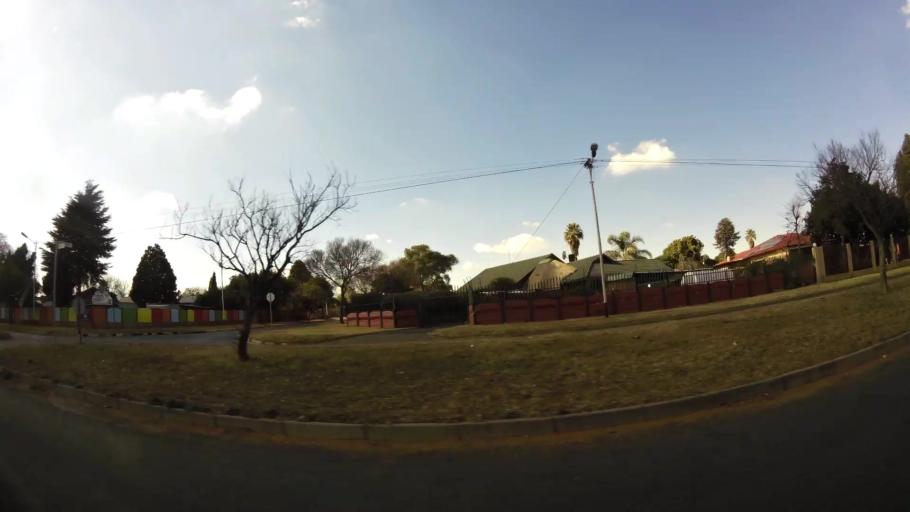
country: ZA
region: Gauteng
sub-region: City of Johannesburg Metropolitan Municipality
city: Roodepoort
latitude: -26.1368
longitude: 27.8297
